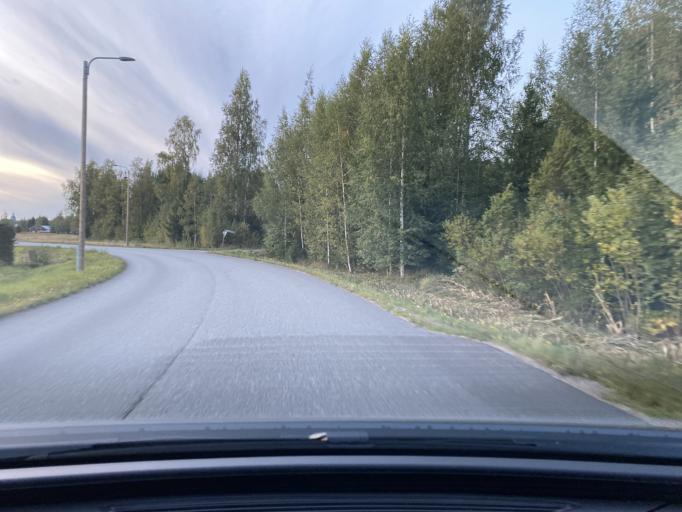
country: FI
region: Satakunta
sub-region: Pori
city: Huittinen
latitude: 61.1717
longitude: 22.7151
